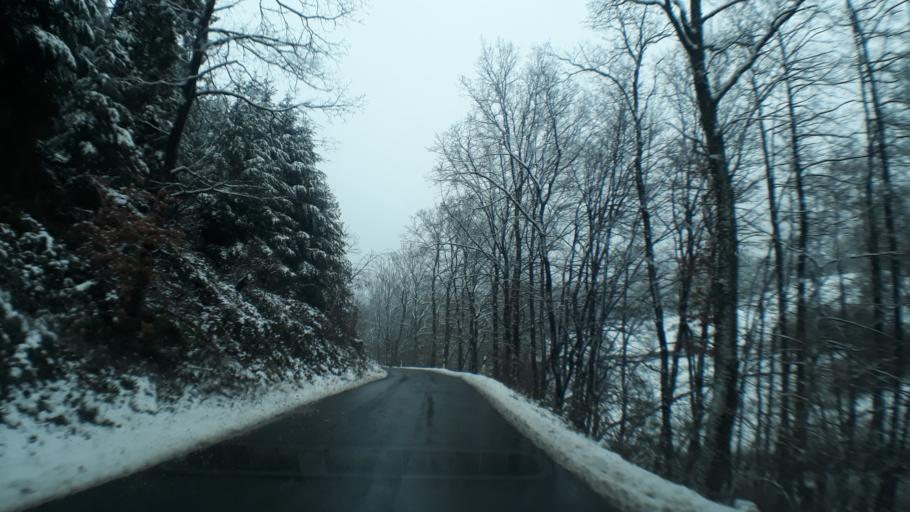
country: DE
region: North Rhine-Westphalia
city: Stolberg
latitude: 50.7362
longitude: 6.2816
